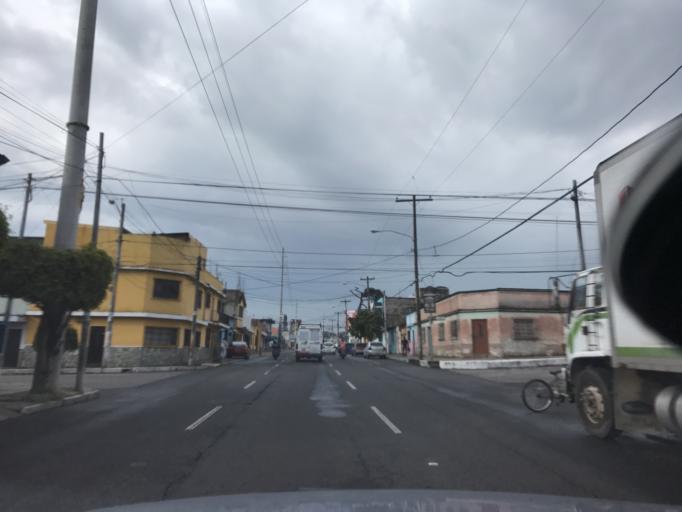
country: GT
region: Guatemala
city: Guatemala City
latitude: 14.6027
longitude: -90.5381
